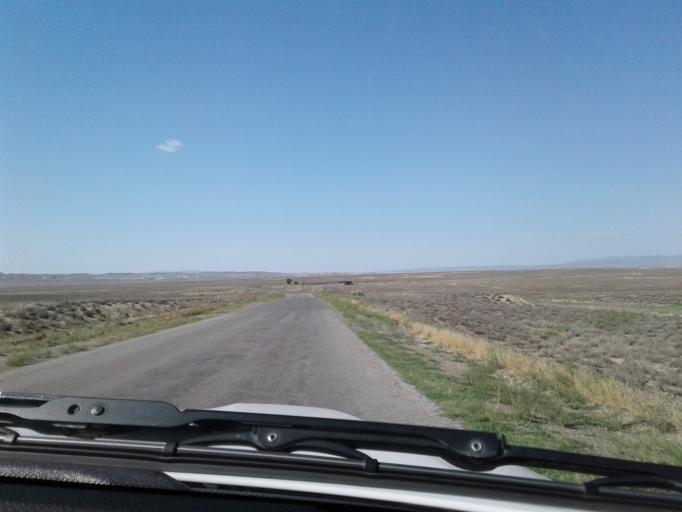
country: TM
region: Balkan
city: Magtymguly
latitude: 38.5950
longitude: 56.1939
